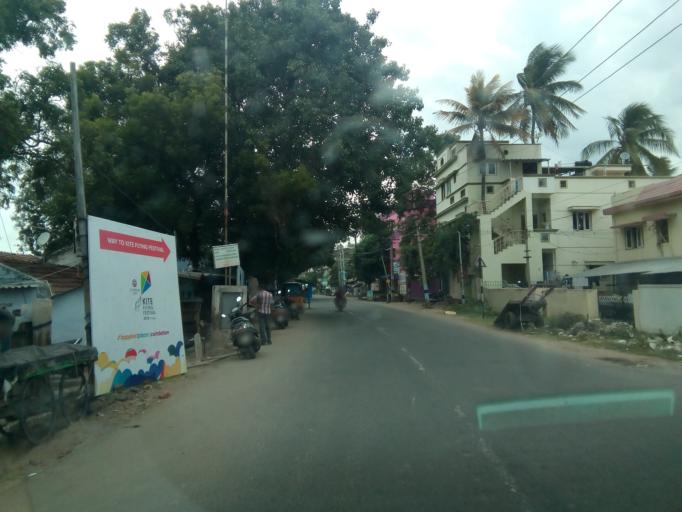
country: IN
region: Tamil Nadu
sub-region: Coimbatore
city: Coimbatore
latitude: 11.0060
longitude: 76.9421
